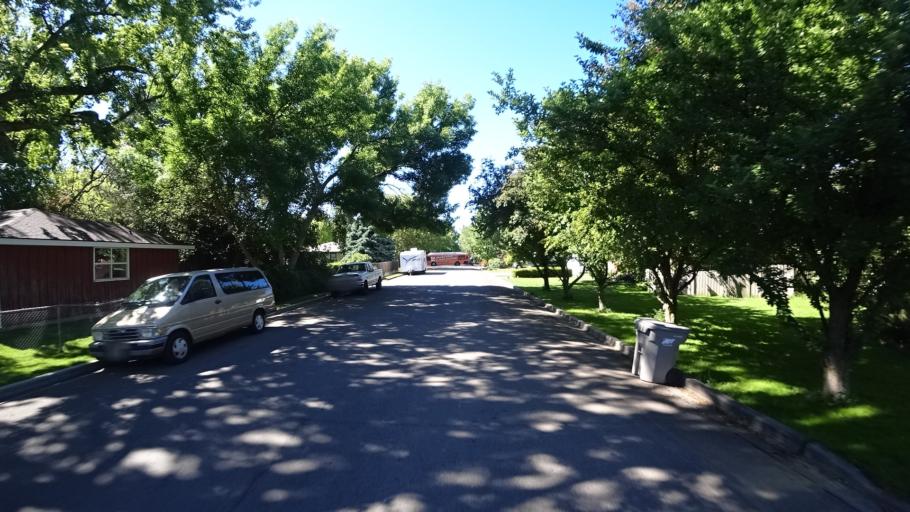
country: US
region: Idaho
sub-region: Ada County
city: Garden City
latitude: 43.6489
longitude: -116.2284
